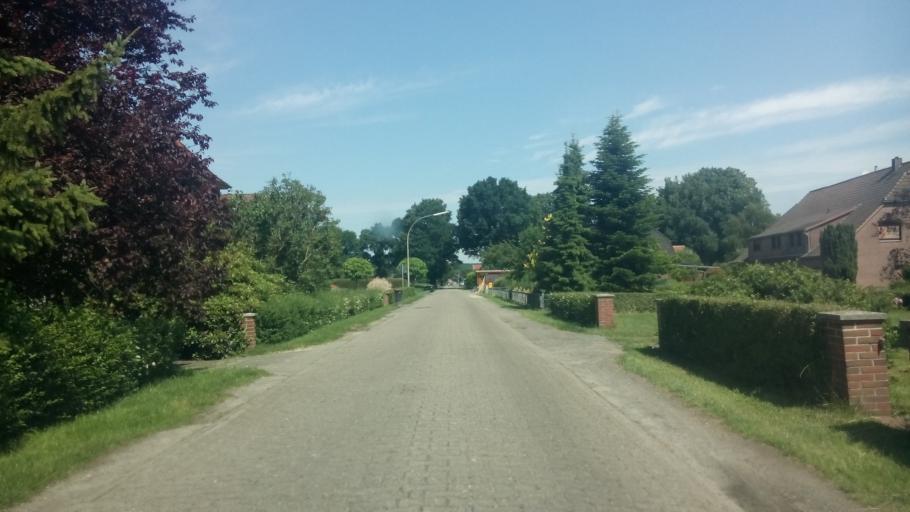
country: DE
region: Lower Saxony
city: Osterholz-Scharmbeck
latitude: 53.2630
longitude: 8.8215
